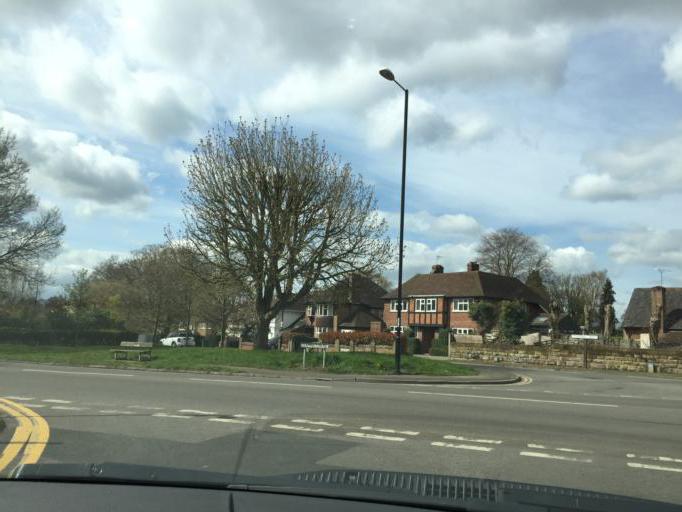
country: GB
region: England
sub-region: Coventry
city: Coventry
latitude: 52.3899
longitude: -1.5156
